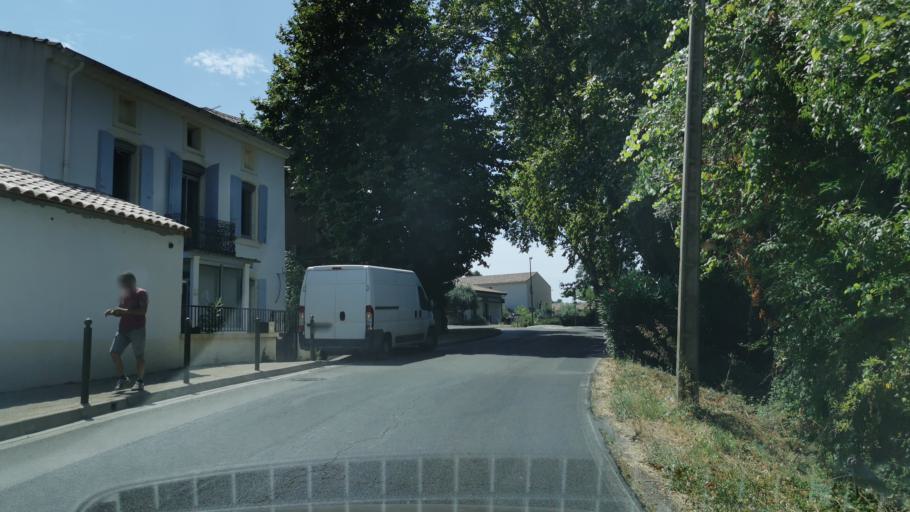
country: FR
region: Languedoc-Roussillon
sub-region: Departement de l'Aude
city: Bize-Minervois
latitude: 43.3133
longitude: 2.8710
